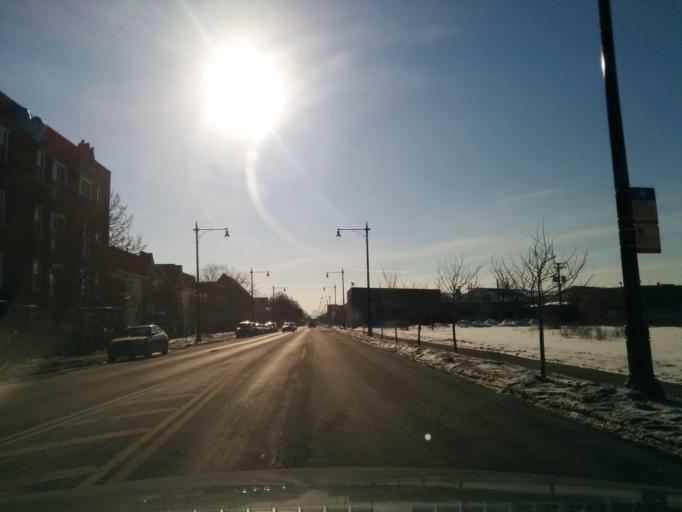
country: US
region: Illinois
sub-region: Cook County
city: Lincolnwood
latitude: 41.9488
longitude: -87.7397
